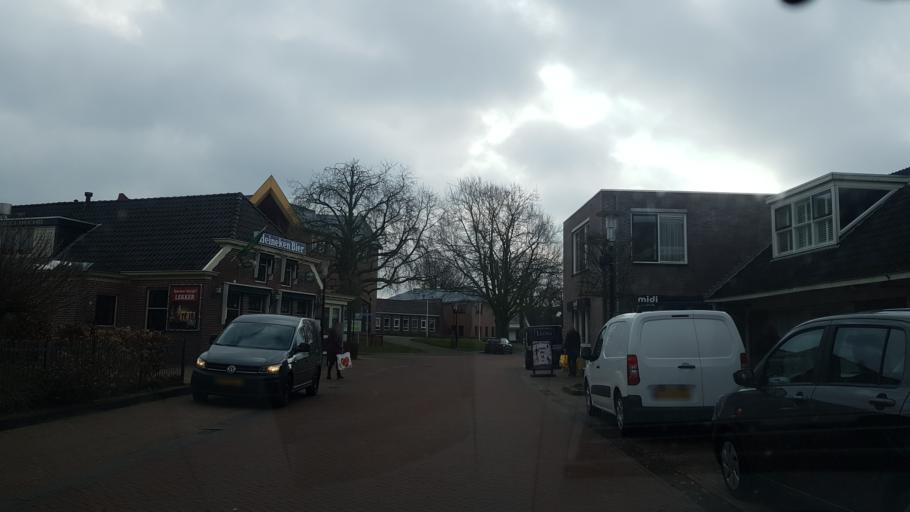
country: NL
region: Drenthe
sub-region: Gemeente Hoogeveen
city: Hoogeveen
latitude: 52.6755
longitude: 6.4293
